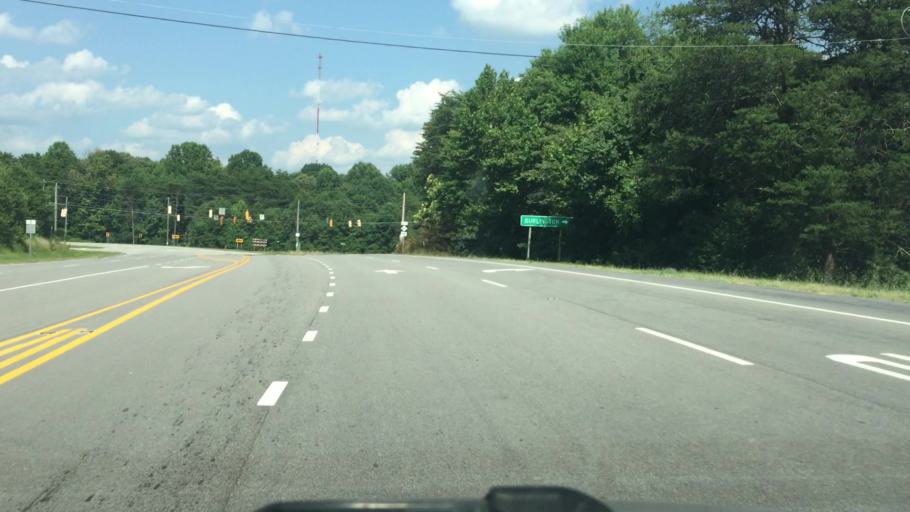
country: US
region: North Carolina
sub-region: Rockingham County
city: Reidsville
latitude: 36.3131
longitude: -79.6320
